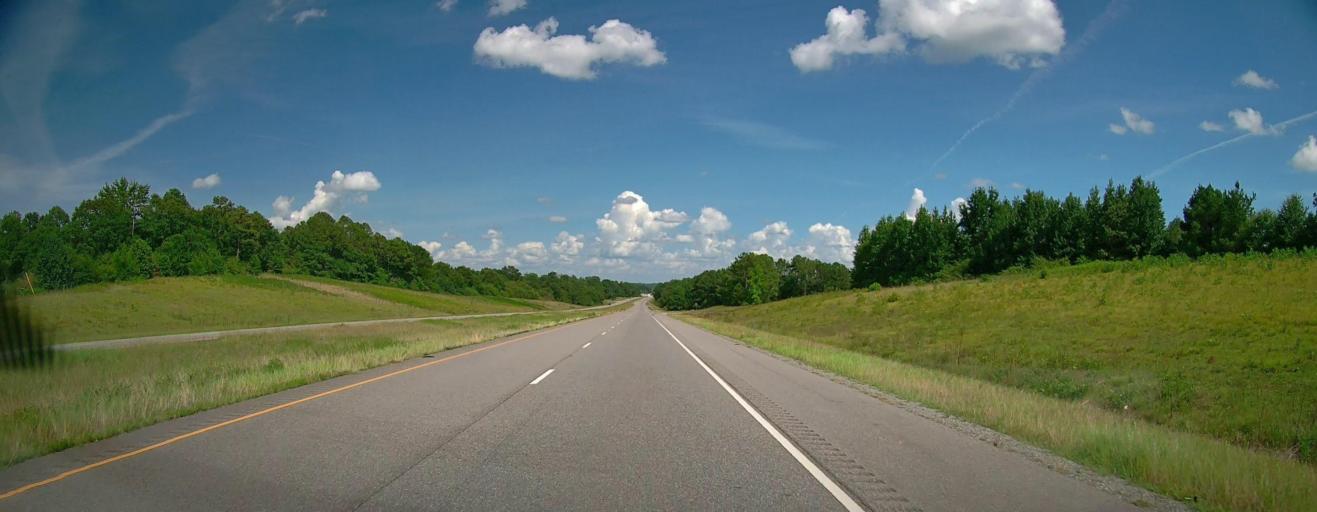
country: US
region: Alabama
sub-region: Pickens County
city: Reform
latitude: 33.3901
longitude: -88.0409
